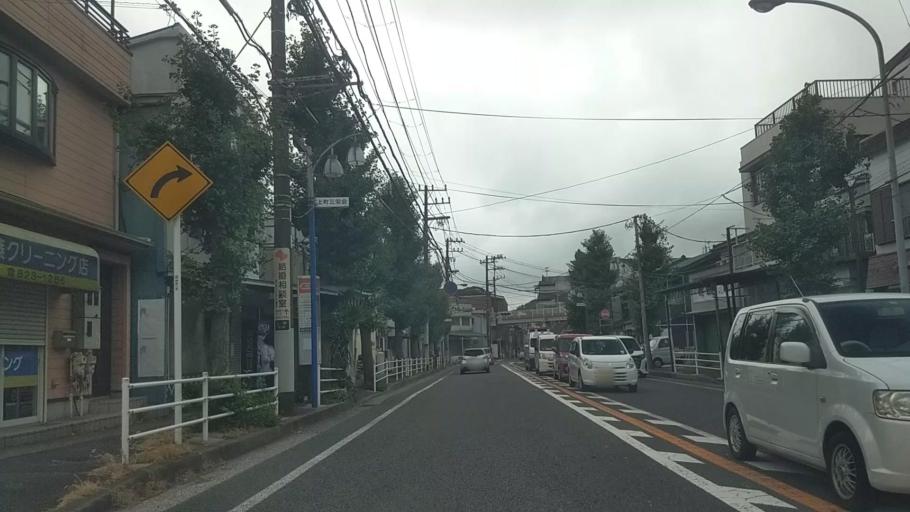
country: JP
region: Kanagawa
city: Yokosuka
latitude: 35.2703
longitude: 139.6717
